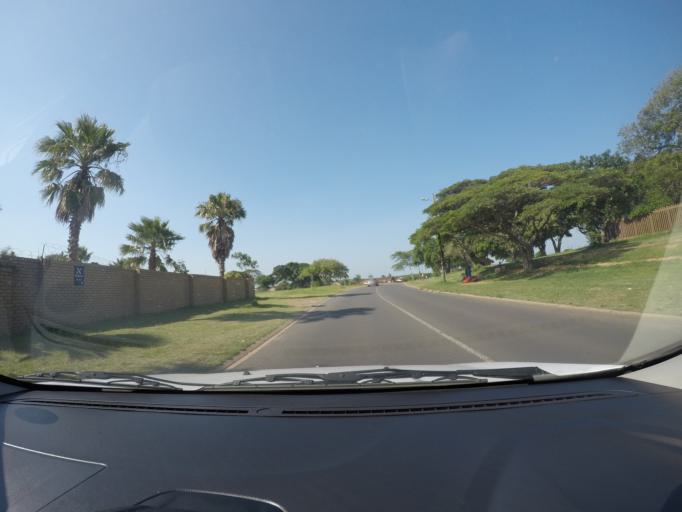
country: ZA
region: KwaZulu-Natal
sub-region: uThungulu District Municipality
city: Richards Bay
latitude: -28.7215
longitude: 32.0412
